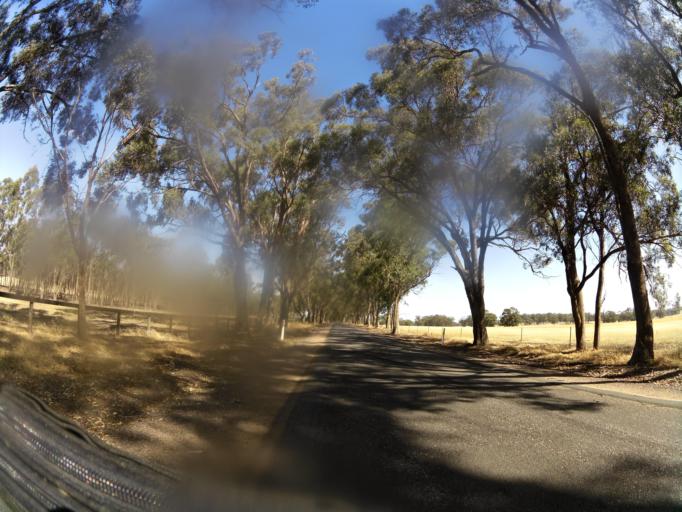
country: AU
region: Victoria
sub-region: Campaspe
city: Kyabram
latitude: -36.8868
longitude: 145.1004
